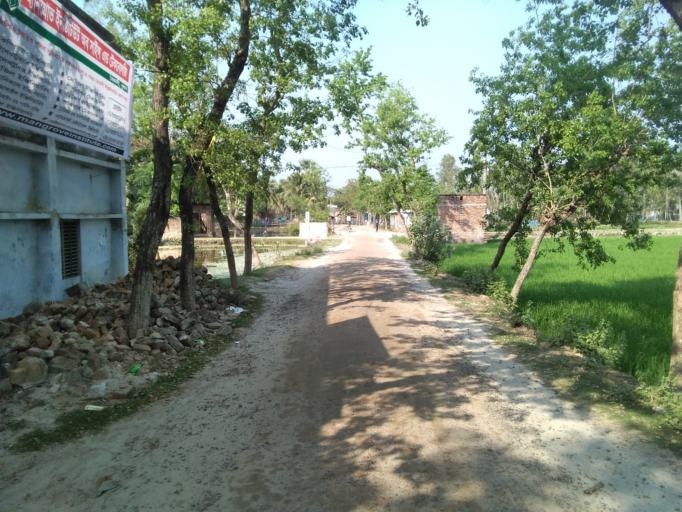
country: IN
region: West Bengal
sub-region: North 24 Parganas
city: Taki
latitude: 22.5244
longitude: 88.9796
